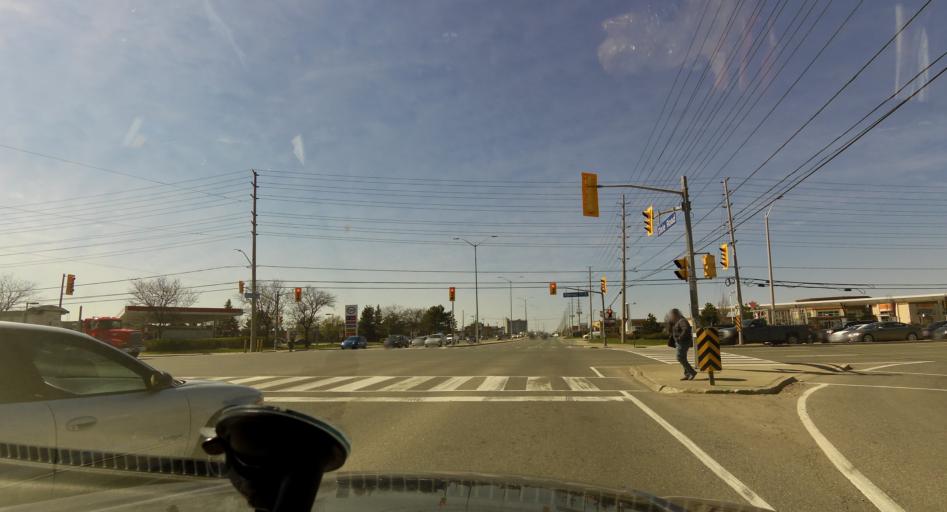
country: CA
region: Ontario
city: Etobicoke
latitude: 43.6357
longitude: -79.6204
